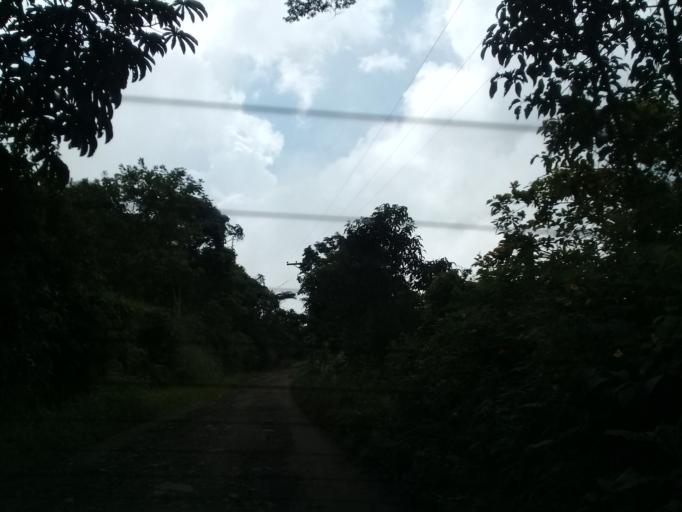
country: CO
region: Cundinamarca
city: Quipile
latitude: 4.7195
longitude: -74.5519
